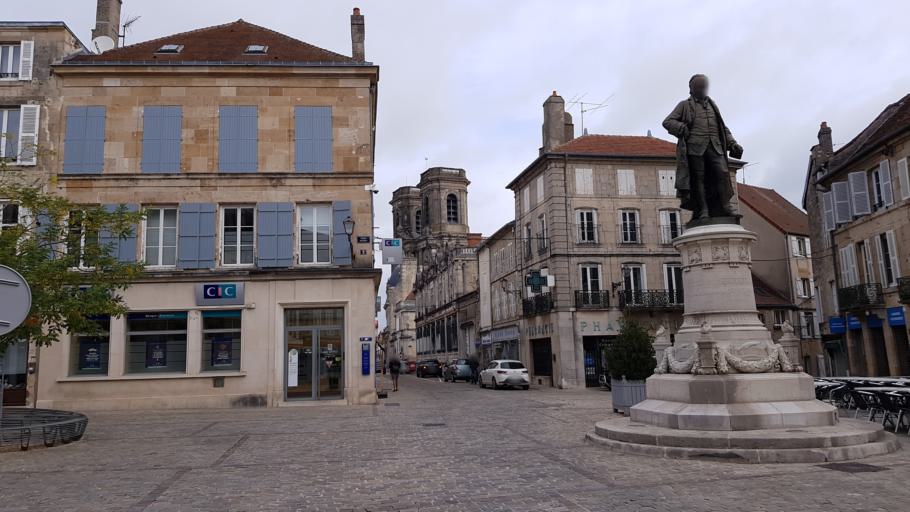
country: FR
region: Champagne-Ardenne
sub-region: Departement de la Haute-Marne
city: Langres
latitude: 47.8627
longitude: 5.3339
